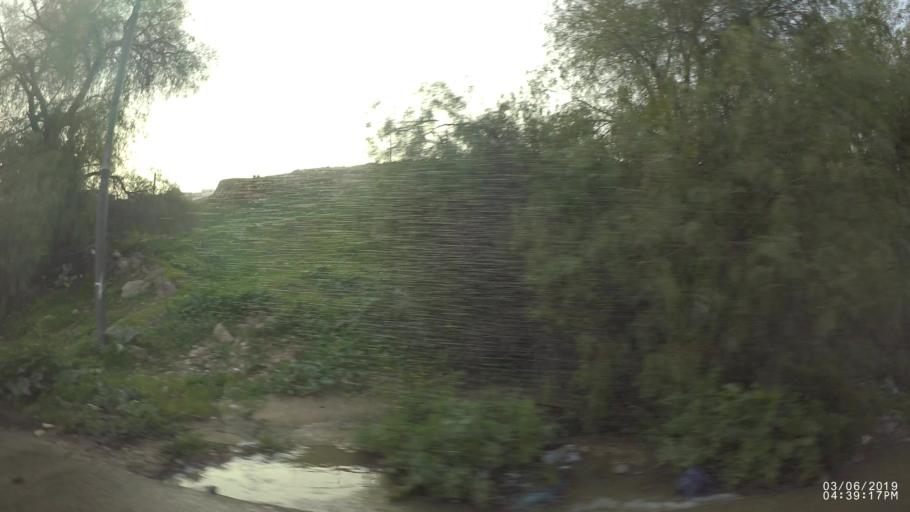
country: JO
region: Amman
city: Amman
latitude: 31.9869
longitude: 35.9767
